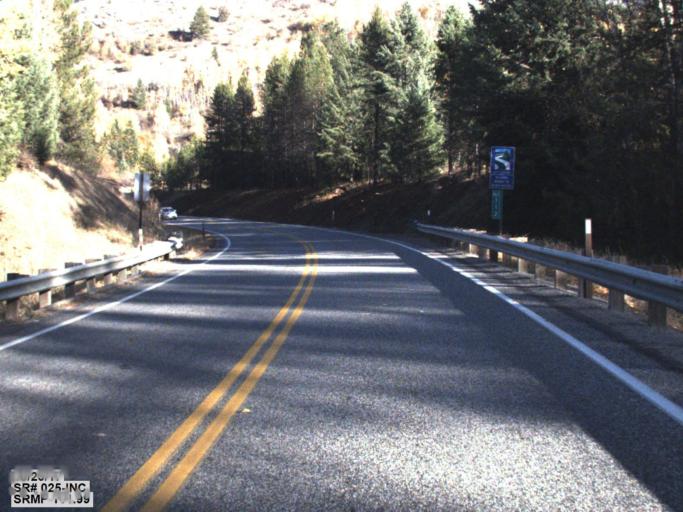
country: CA
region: British Columbia
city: Rossland
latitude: 48.8990
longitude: -117.7988
